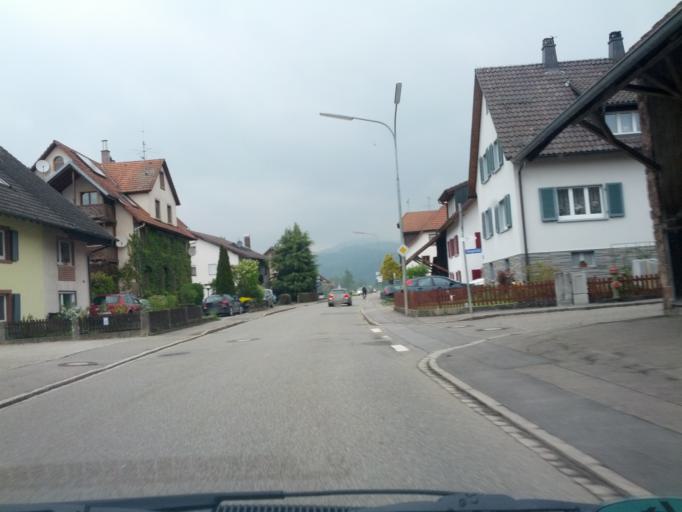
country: DE
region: Baden-Wuerttemberg
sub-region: Freiburg Region
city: Schopfheim
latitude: 47.6632
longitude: 7.8007
